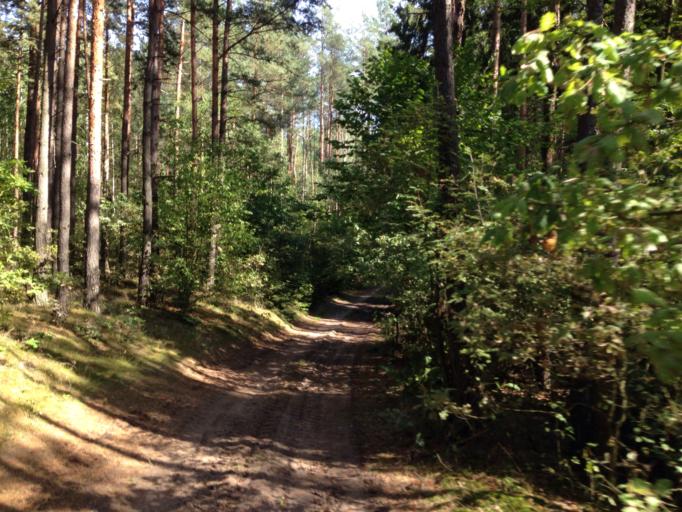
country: PL
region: Warmian-Masurian Voivodeship
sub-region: Powiat dzialdowski
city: Lidzbark
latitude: 53.2071
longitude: 19.7548
